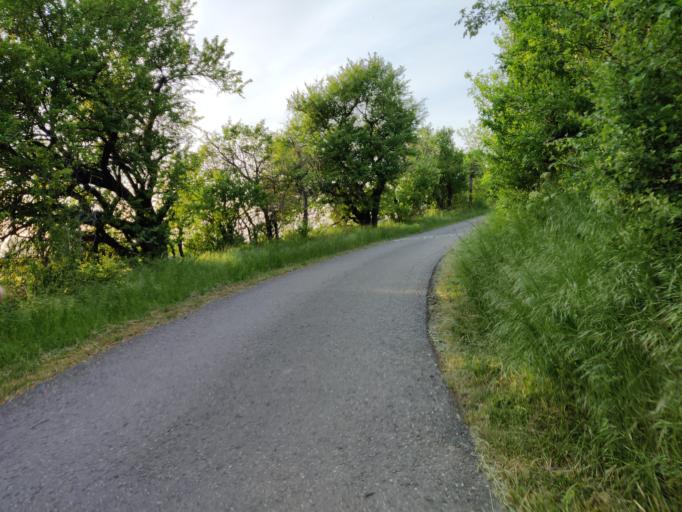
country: DE
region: Saxony-Anhalt
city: Balgstadt
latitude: 51.2170
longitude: 11.7094
